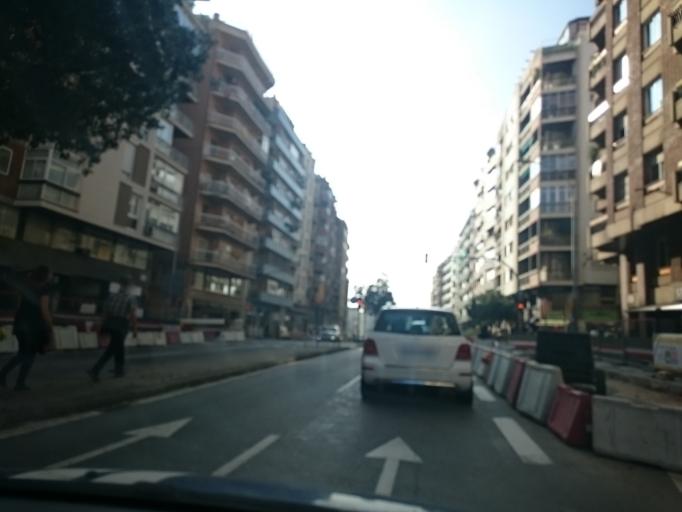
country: ES
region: Catalonia
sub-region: Provincia de Barcelona
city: Gracia
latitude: 41.4087
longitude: 2.1527
